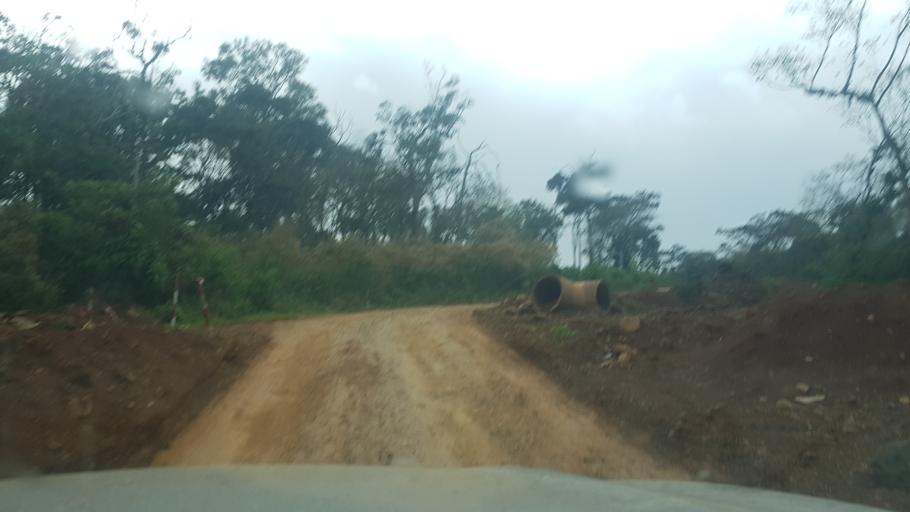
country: ET
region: Oromiya
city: Gore
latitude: 7.8846
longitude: 35.4859
